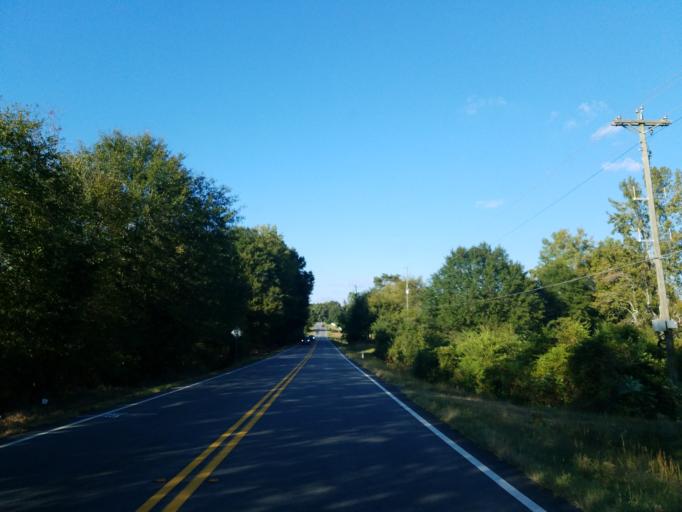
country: US
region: Georgia
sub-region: Bartow County
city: Emerson
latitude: 34.0552
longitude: -84.8282
